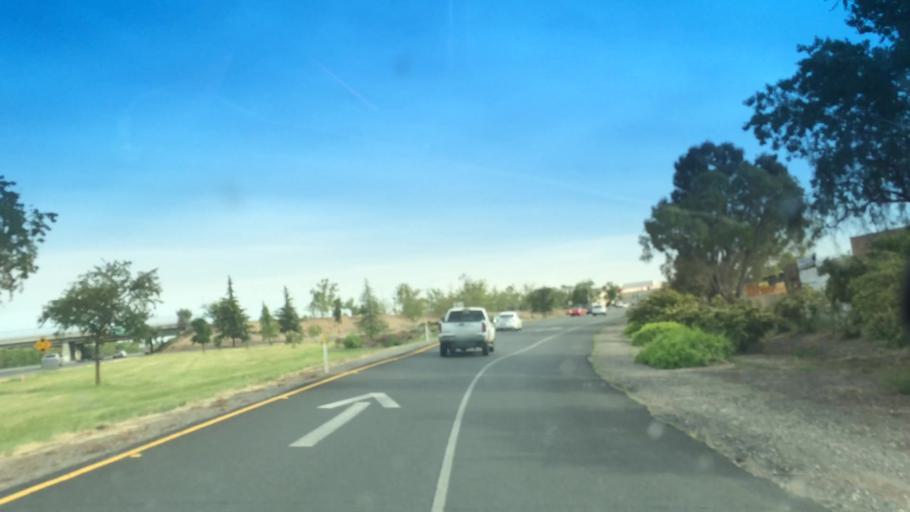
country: US
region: California
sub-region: Butte County
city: Chico
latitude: 39.7278
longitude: -121.8111
